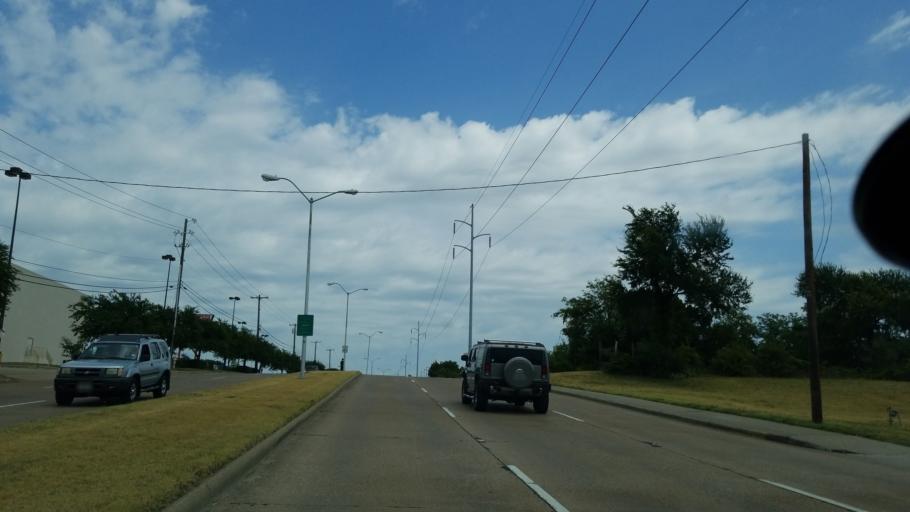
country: US
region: Texas
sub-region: Dallas County
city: Duncanville
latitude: 32.6621
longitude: -96.8440
